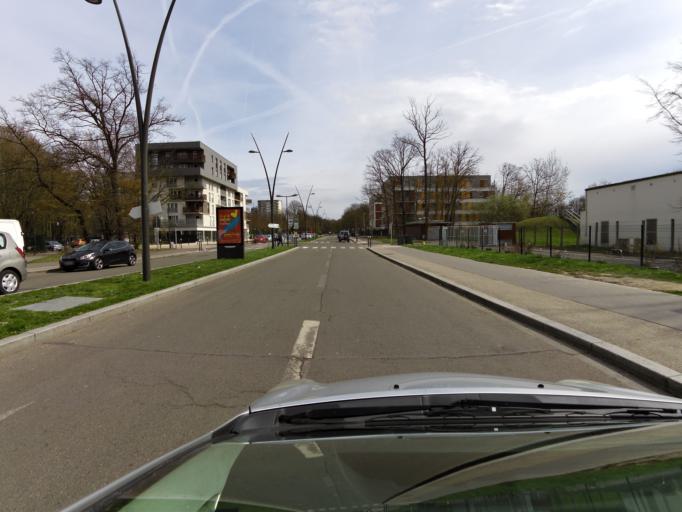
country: FR
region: Ile-de-France
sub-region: Departement de Seine-Saint-Denis
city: Tremblay-en-France
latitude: 48.9459
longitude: 2.5688
